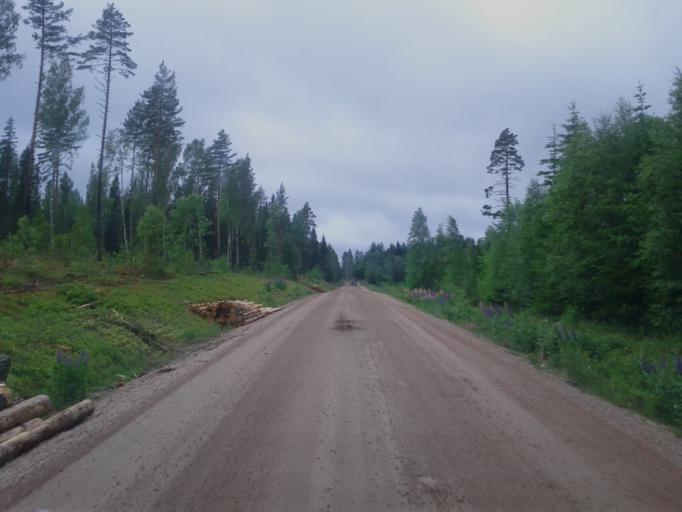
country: SE
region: Gaevleborg
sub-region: Hudiksvalls Kommun
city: Delsbo
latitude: 62.1408
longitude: 16.6223
